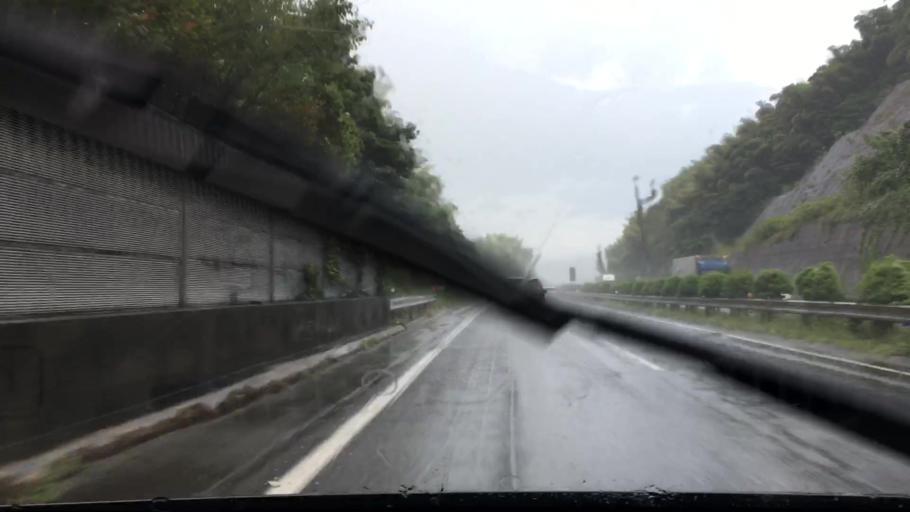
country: JP
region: Fukuoka
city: Kitakyushu
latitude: 33.8081
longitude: 130.8214
